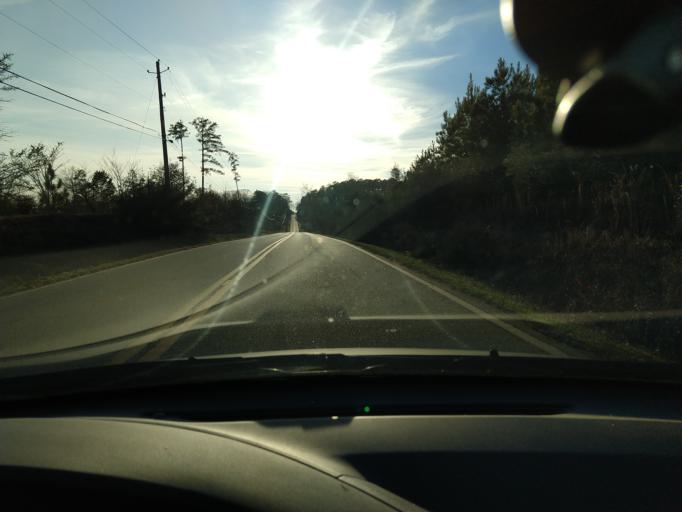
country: US
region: Georgia
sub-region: Sumter County
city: Americus
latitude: 32.0883
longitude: -84.1962
